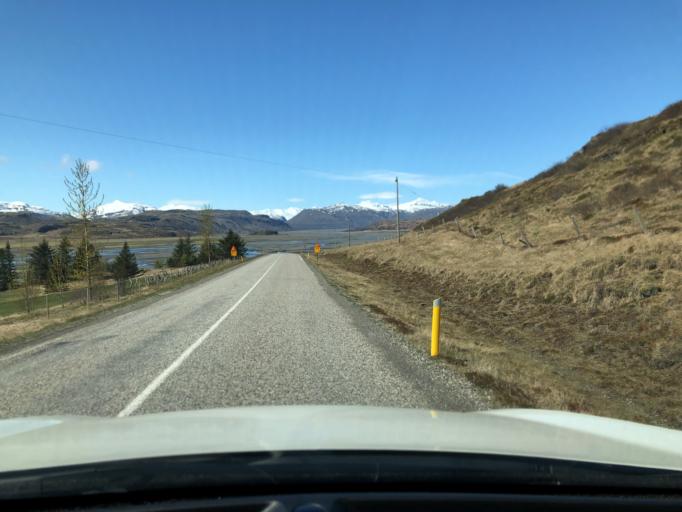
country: IS
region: East
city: Hoefn
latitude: 64.4215
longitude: -14.8763
